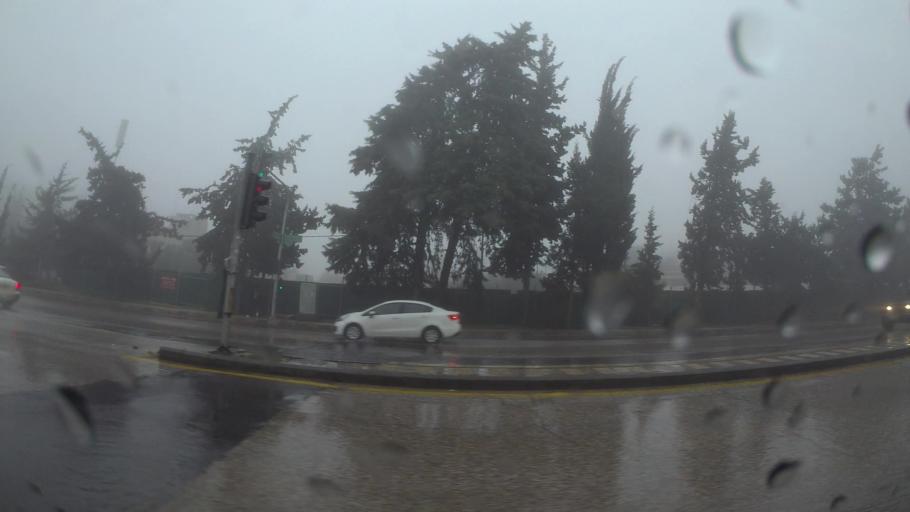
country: JO
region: Amman
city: Al Jubayhah
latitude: 32.0061
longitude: 35.8792
